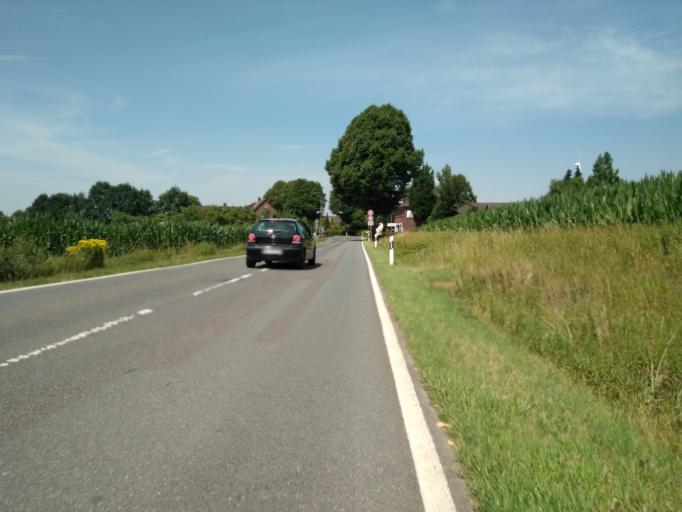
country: DE
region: North Rhine-Westphalia
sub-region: Regierungsbezirk Dusseldorf
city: Schermbeck
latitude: 51.6439
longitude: 6.8961
